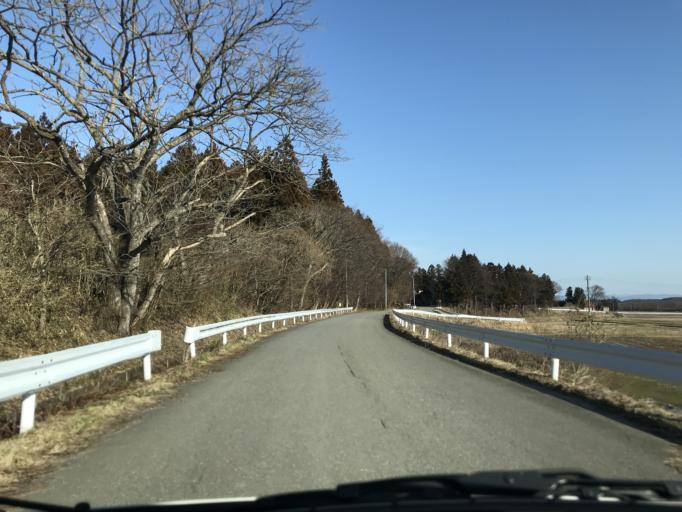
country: JP
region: Iwate
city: Kitakami
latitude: 39.2994
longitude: 141.0062
